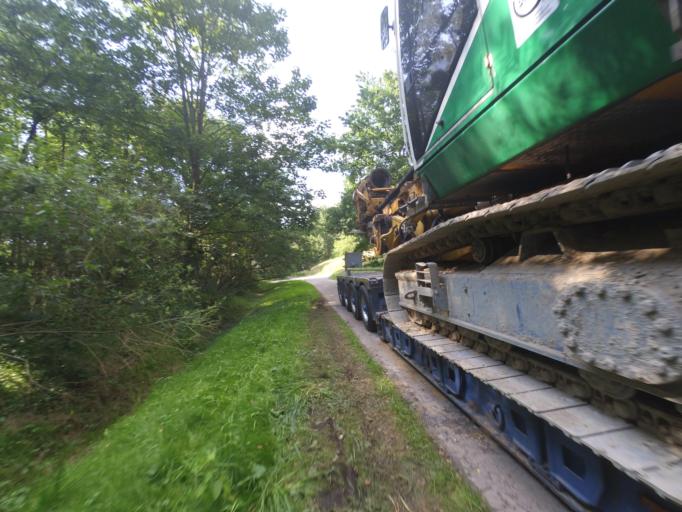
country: DE
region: Schleswig-Holstein
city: Oststeinbek
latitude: 53.5173
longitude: 10.1535
